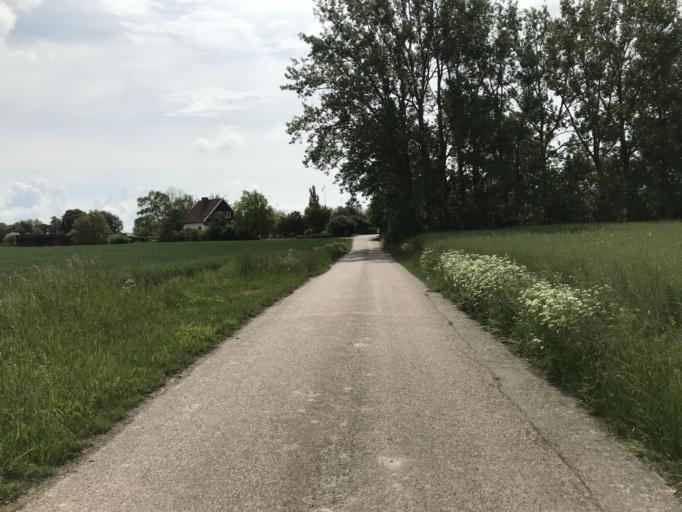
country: SE
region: Skane
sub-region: Landskrona
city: Landskrona
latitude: 55.9061
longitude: 12.8474
